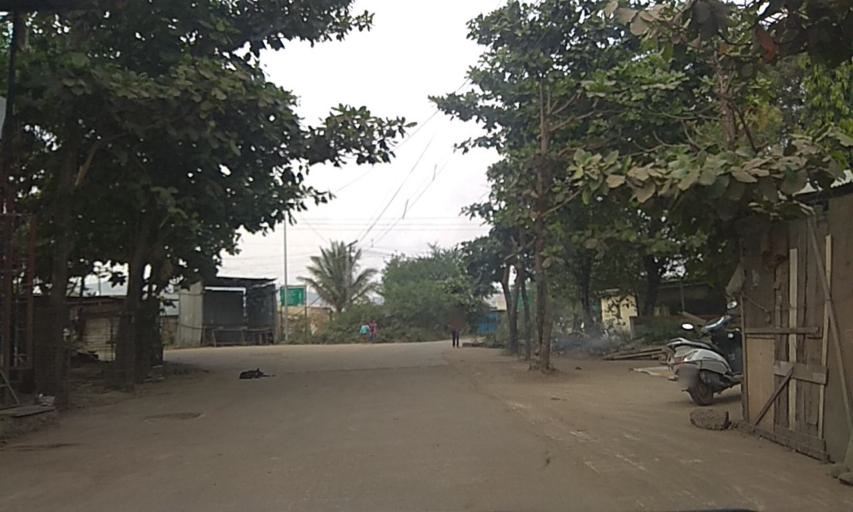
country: IN
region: Maharashtra
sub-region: Pune Division
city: Pimpri
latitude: 18.5769
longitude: 73.7091
